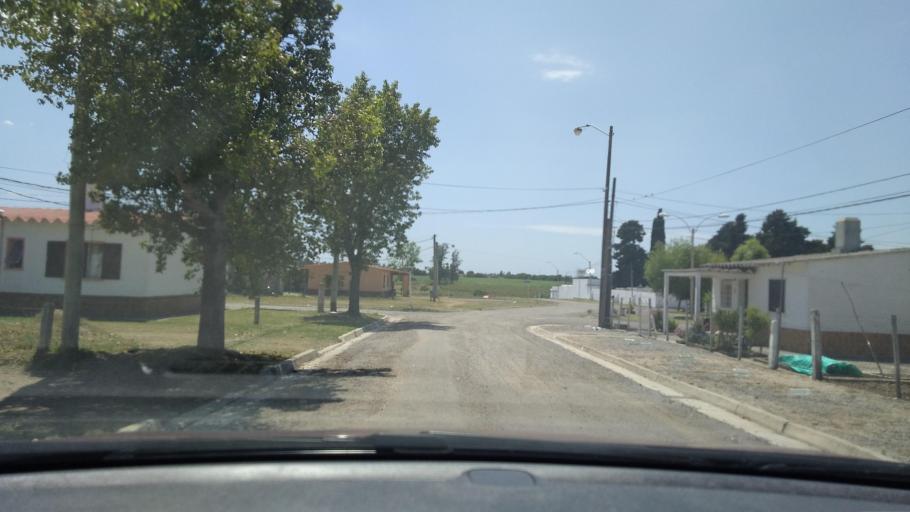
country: UY
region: Canelones
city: Tala
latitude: -34.2042
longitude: -55.7421
